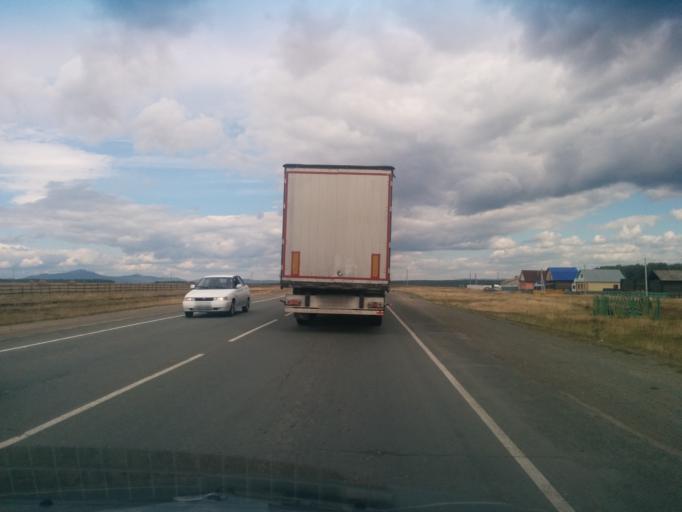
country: RU
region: Bashkortostan
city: Lomovka
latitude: 53.8806
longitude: 58.1110
